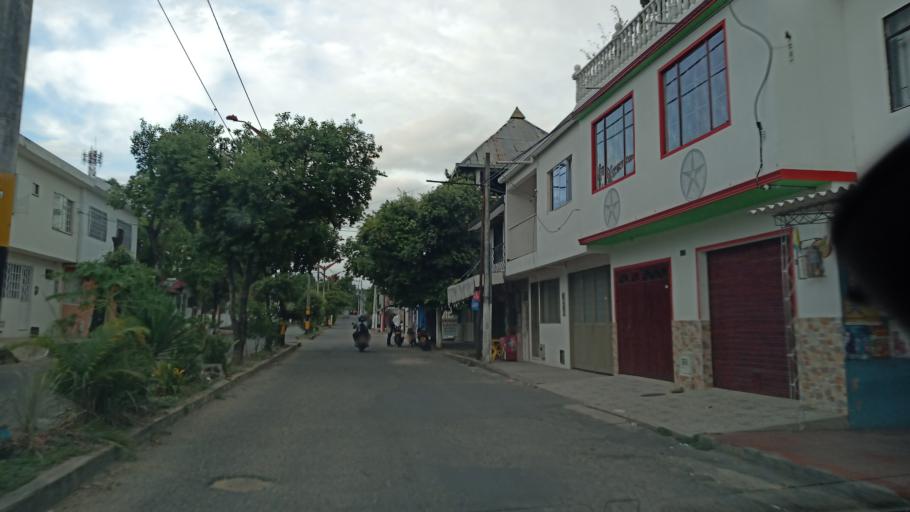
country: CO
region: Tolima
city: Melgar
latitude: 4.1997
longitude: -74.6501
